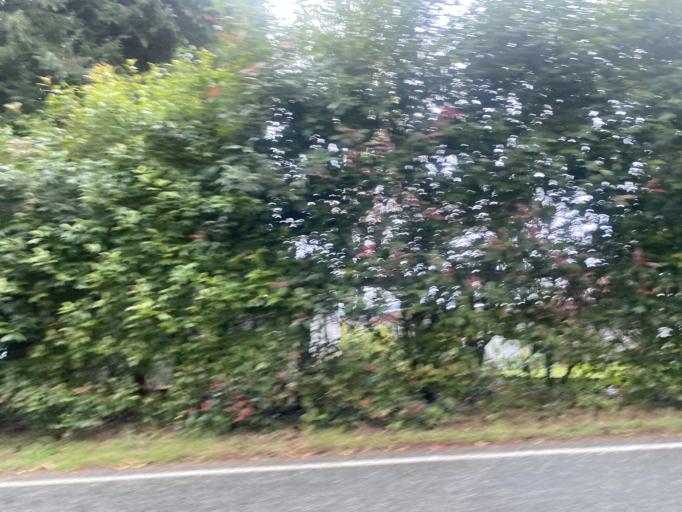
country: US
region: Washington
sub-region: Island County
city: Camano
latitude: 48.0964
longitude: -122.5136
